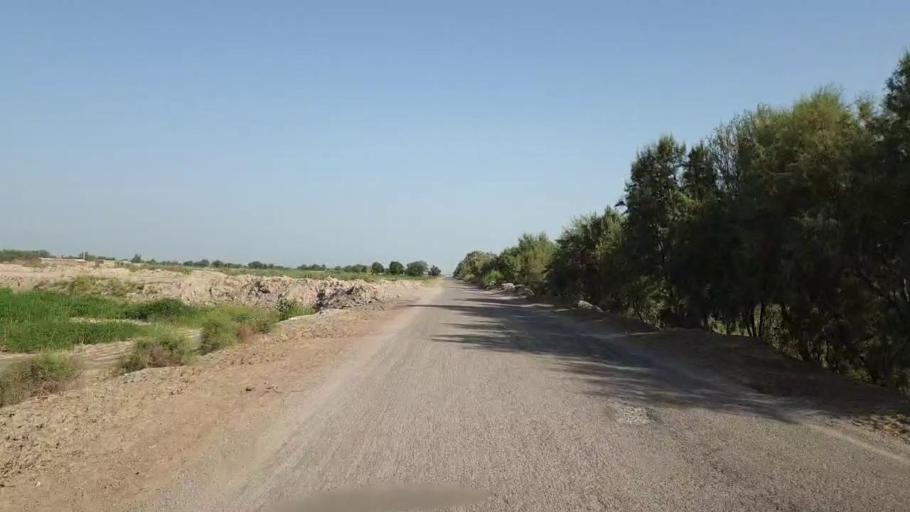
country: PK
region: Sindh
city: Nawabshah
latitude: 26.1582
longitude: 68.4449
